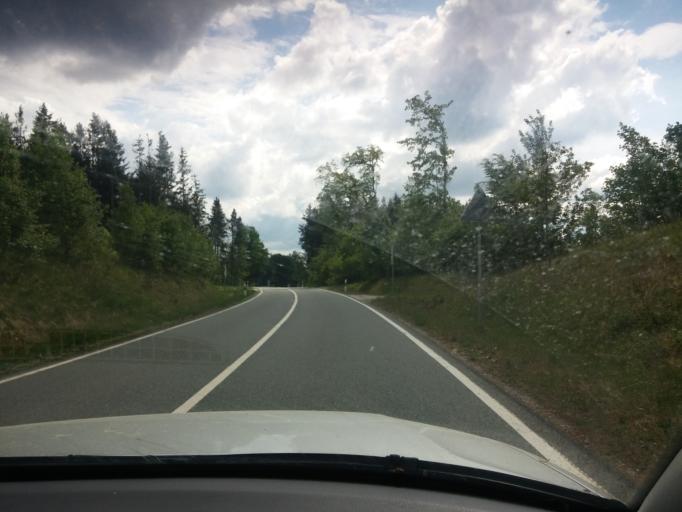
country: DE
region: Bavaria
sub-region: Upper Bavaria
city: Hohenkirchen-Siegertsbrunn
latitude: 48.0084
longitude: 11.7098
